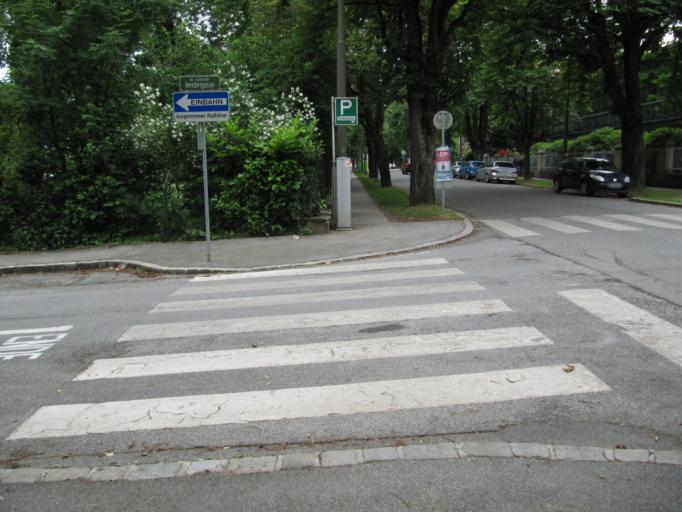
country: AT
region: Styria
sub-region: Graz Stadt
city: Graz
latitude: 47.0799
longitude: 15.4559
